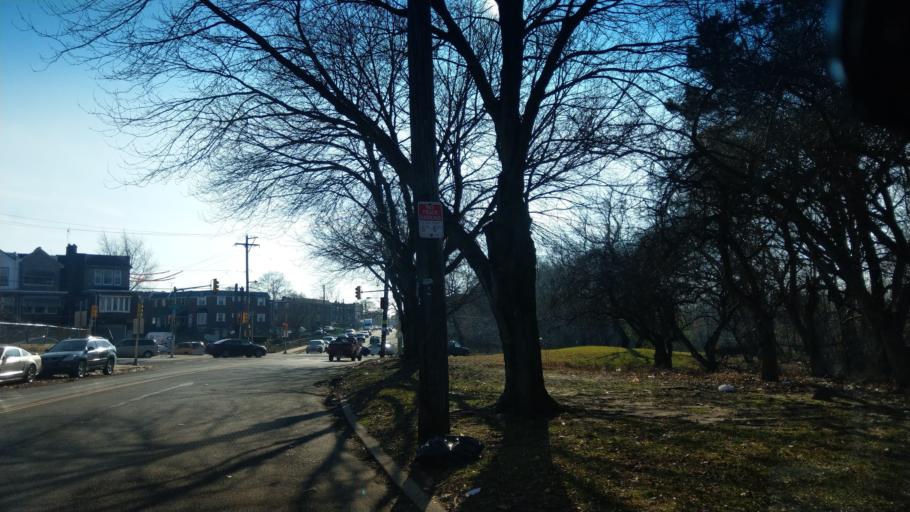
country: US
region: Pennsylvania
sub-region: Montgomery County
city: Rockledge
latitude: 40.0324
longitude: -75.1090
